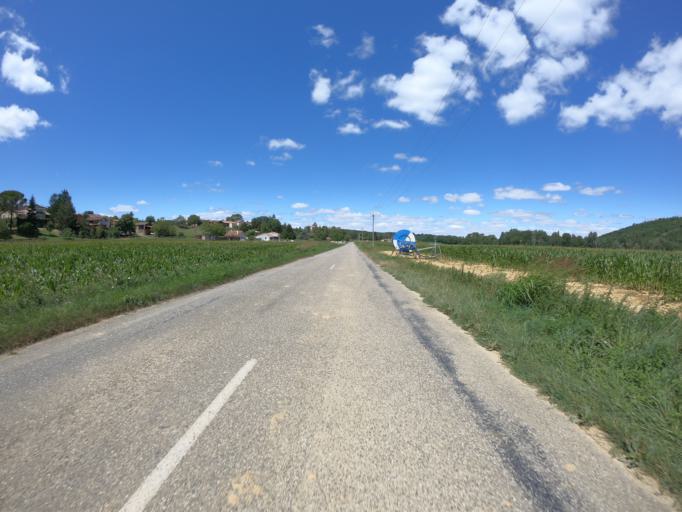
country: FR
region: Midi-Pyrenees
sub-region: Departement de l'Ariege
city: Verniolle
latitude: 43.0609
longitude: 1.7409
